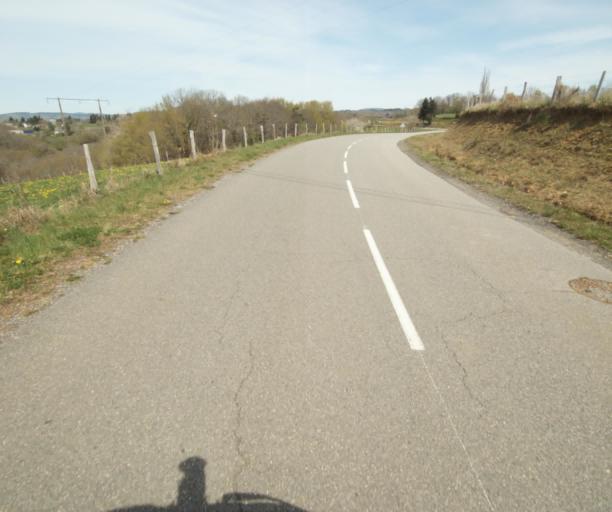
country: FR
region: Limousin
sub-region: Departement de la Correze
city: Naves
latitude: 45.3717
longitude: 1.7997
